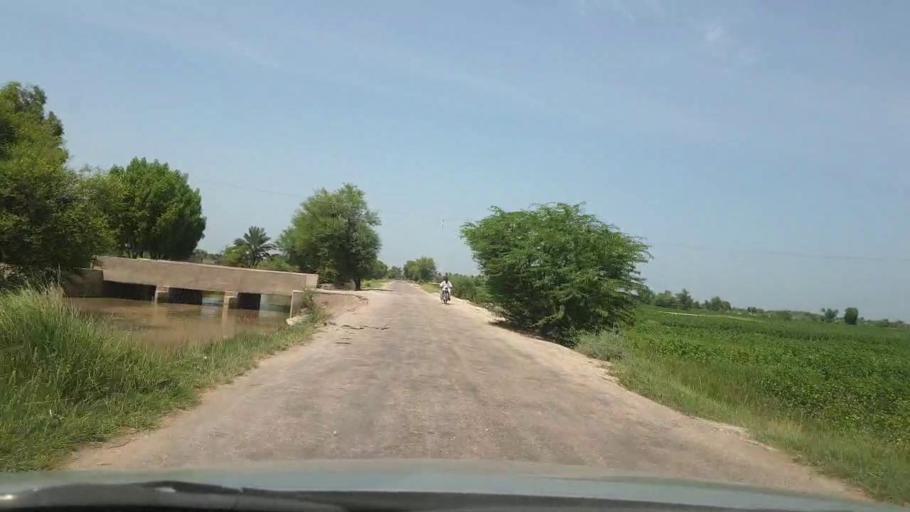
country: PK
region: Sindh
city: Pano Aqil
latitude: 27.6751
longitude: 69.1091
